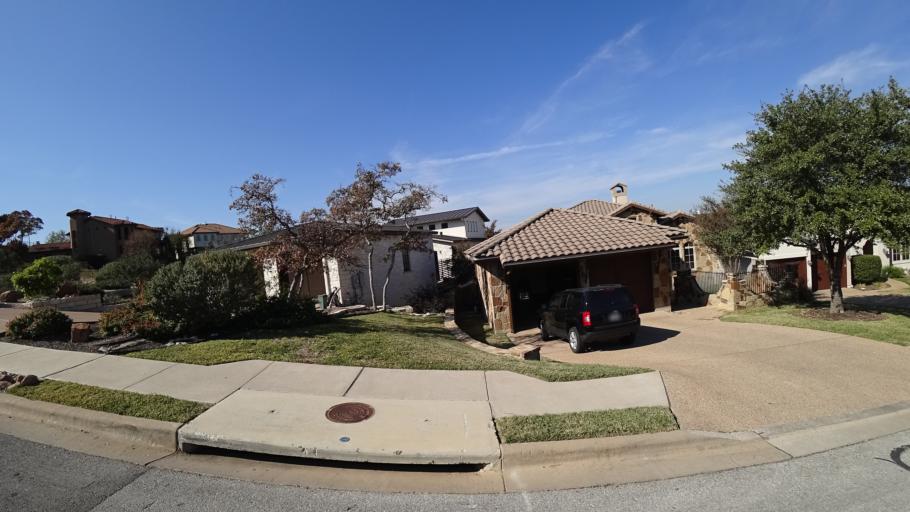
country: US
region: Texas
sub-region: Williamson County
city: Jollyville
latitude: 30.3707
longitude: -97.7805
